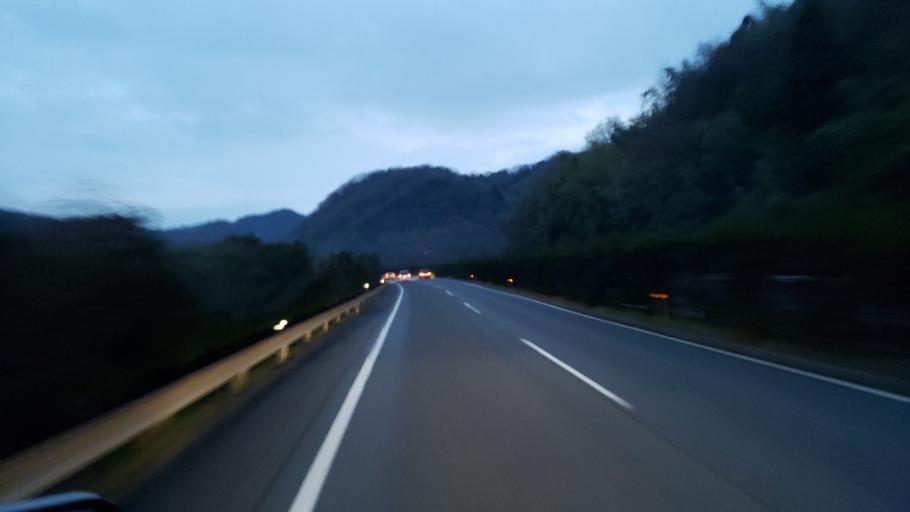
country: JP
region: Hyogo
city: Himeji
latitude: 34.8678
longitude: 134.7401
